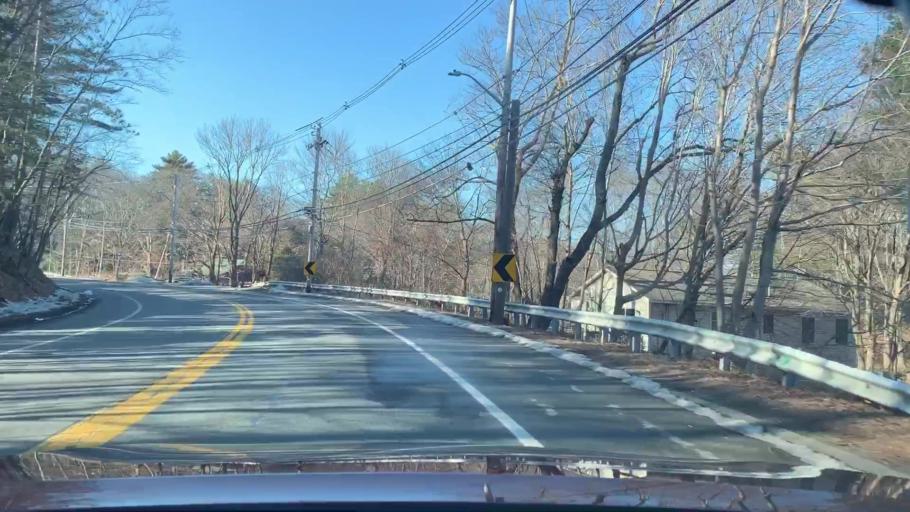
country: US
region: Massachusetts
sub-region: Essex County
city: Gloucester
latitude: 42.6154
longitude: -70.6954
